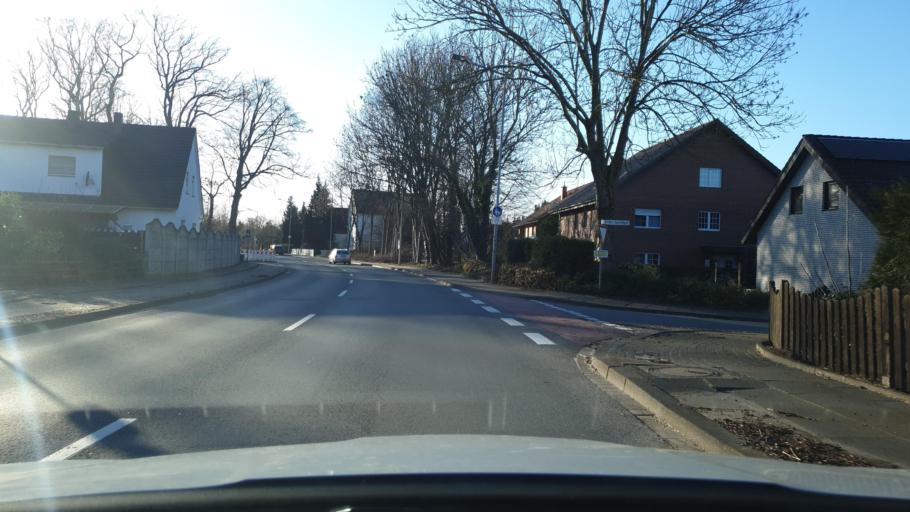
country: DE
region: North Rhine-Westphalia
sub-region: Regierungsbezirk Detmold
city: Kirchlengern
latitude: 52.2051
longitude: 8.6570
